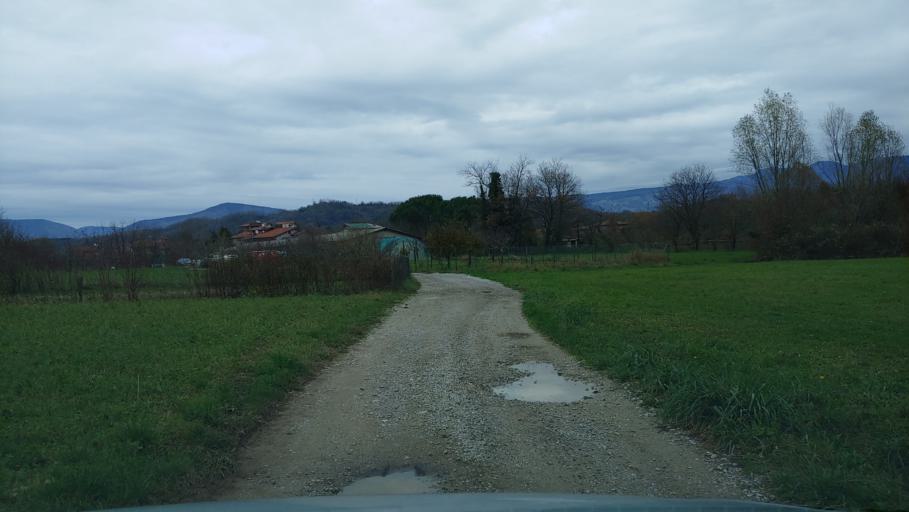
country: SI
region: Sempeter-Vrtojba
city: Vrtojba
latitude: 45.9107
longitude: 13.6390
